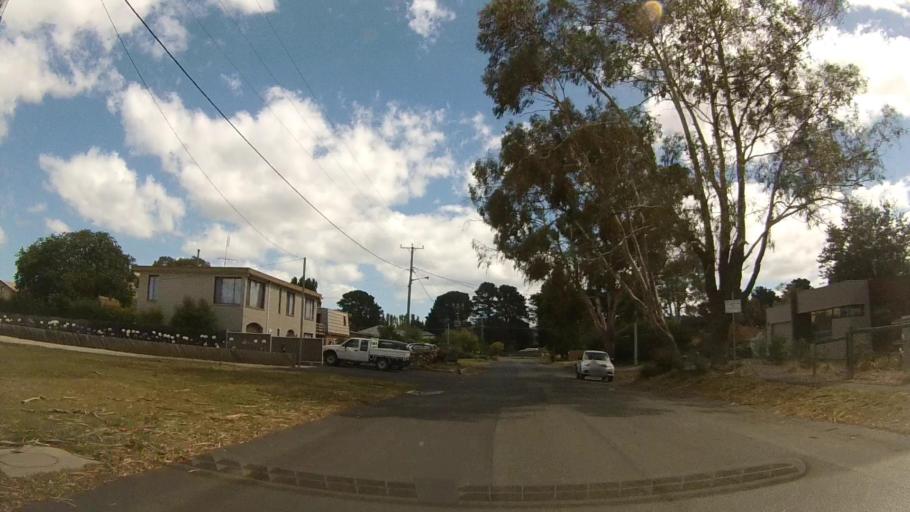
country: AU
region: Tasmania
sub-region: Clarence
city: Seven Mile Beach
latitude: -42.8582
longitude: 147.5020
